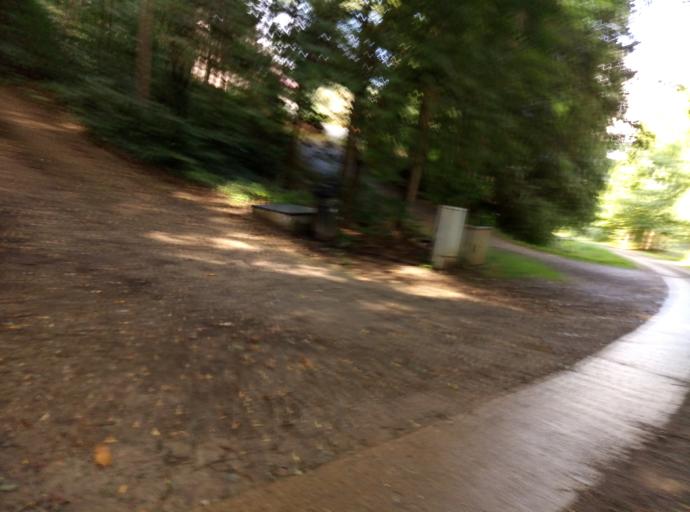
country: BE
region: Flanders
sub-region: Provincie Vlaams-Brabant
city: Holsbeek
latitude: 50.9115
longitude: 4.7400
